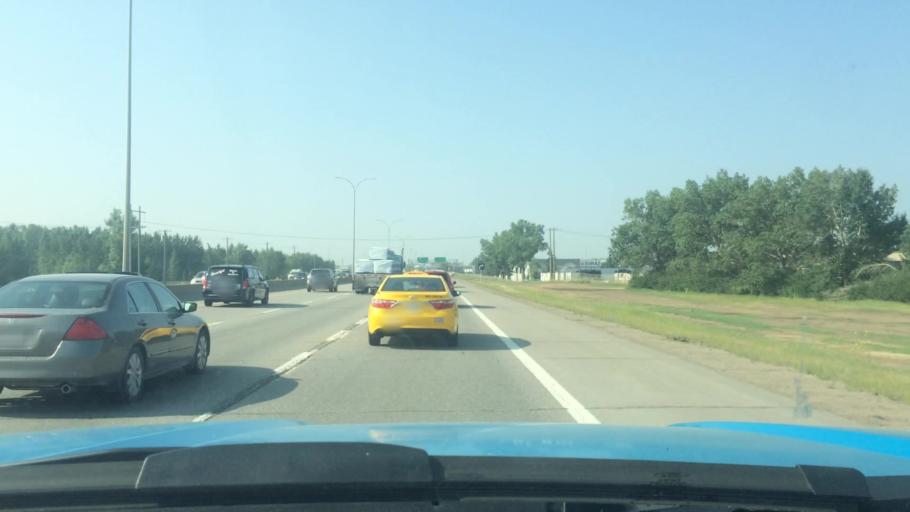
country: CA
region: Alberta
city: Calgary
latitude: 51.0029
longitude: -114.0304
